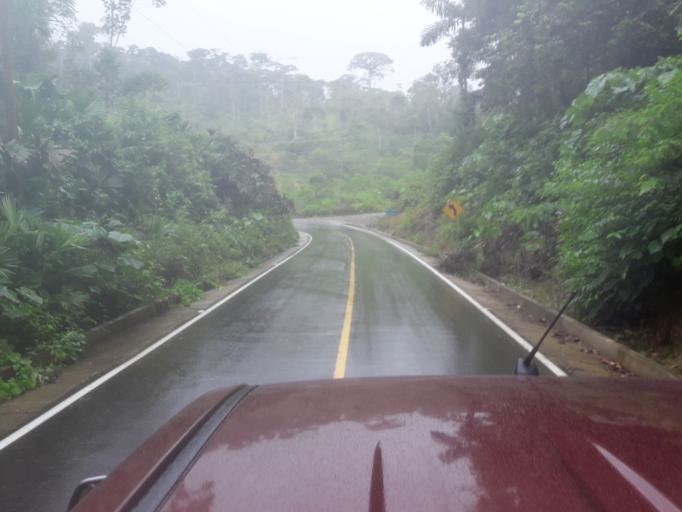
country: EC
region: Napo
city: Tena
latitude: -1.0238
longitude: -77.6625
